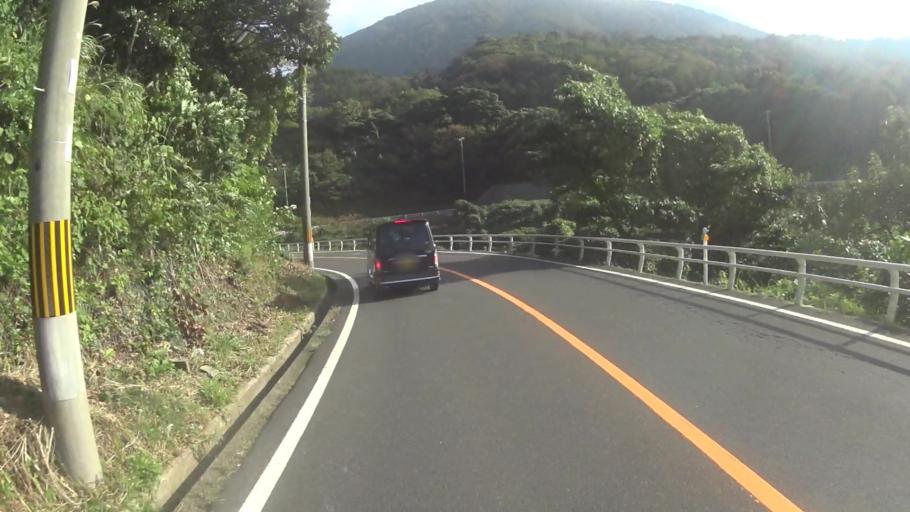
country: JP
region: Kyoto
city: Miyazu
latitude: 35.7474
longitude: 135.1296
